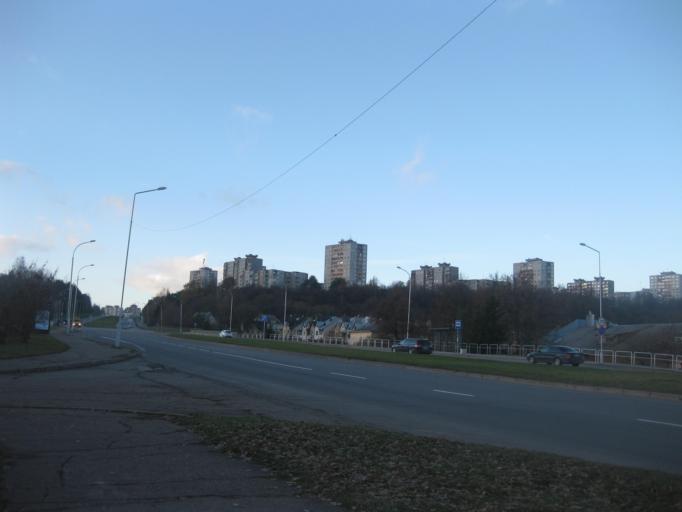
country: LT
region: Kauno apskritis
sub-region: Kaunas
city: Silainiai
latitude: 54.9246
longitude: 23.9066
